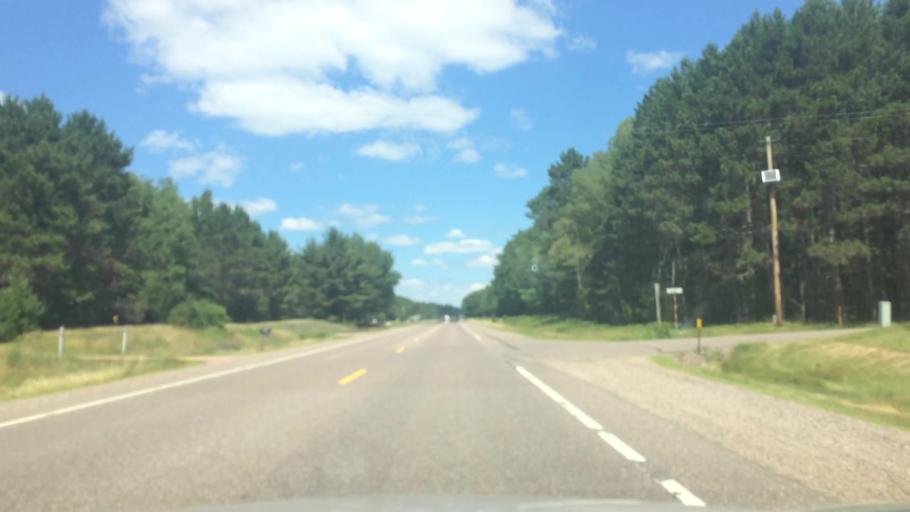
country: US
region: Wisconsin
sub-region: Vilas County
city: Lac du Flambeau
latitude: 45.9733
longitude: -89.6994
